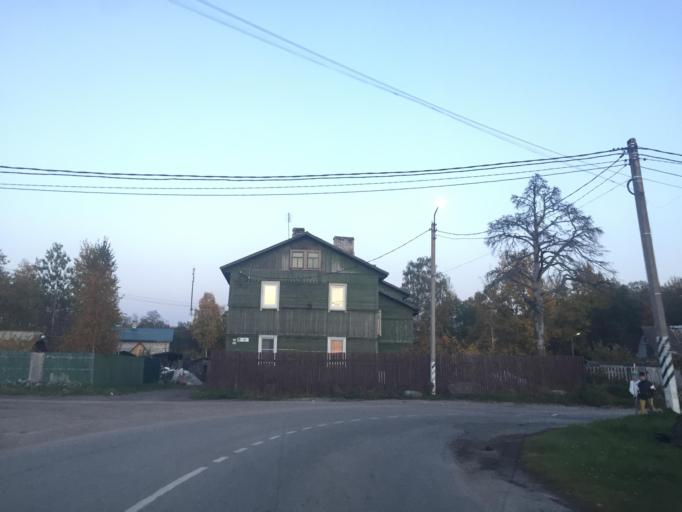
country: RU
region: Leningrad
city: Priozersk
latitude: 61.0335
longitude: 30.1318
